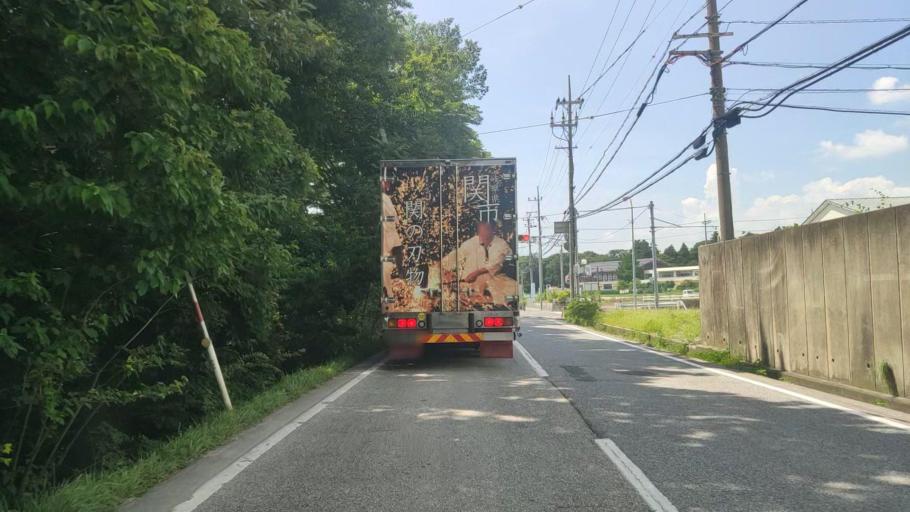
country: JP
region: Shiga Prefecture
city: Nagahama
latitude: 35.3729
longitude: 136.3877
